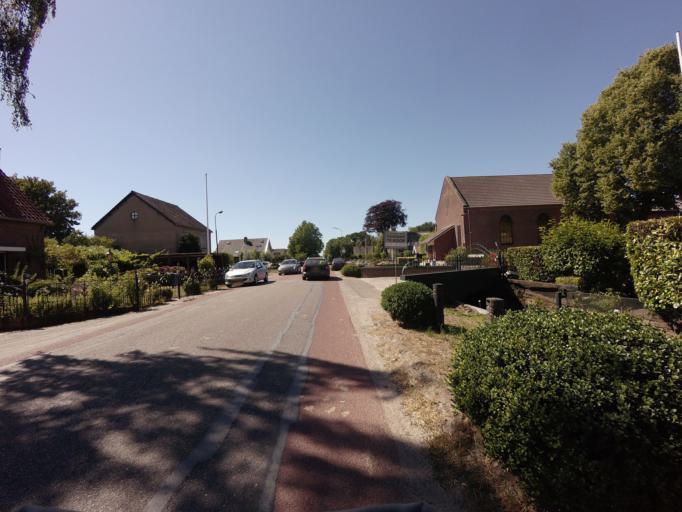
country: NL
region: North Holland
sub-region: Gemeente Wijdemeren
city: Nieuw-Loosdrecht
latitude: 52.1540
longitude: 5.1186
